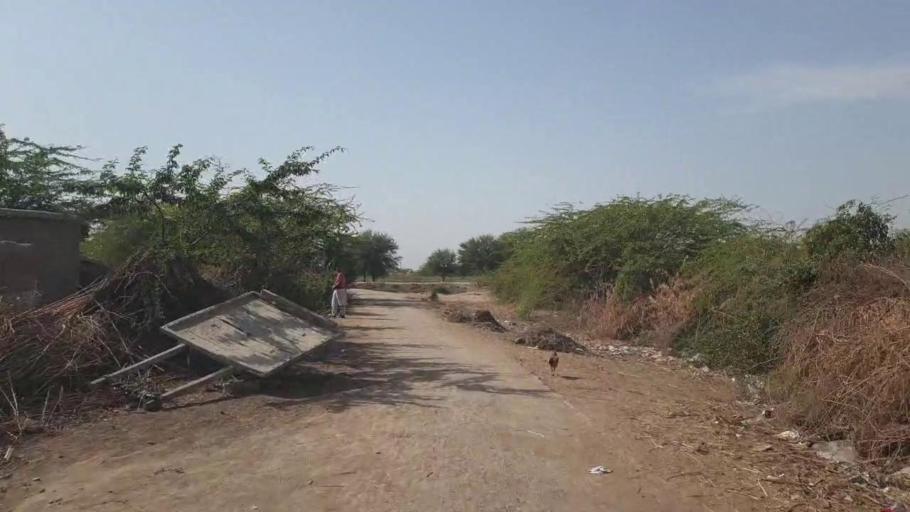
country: PK
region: Sindh
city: Dhoro Naro
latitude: 25.4248
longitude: 69.5685
